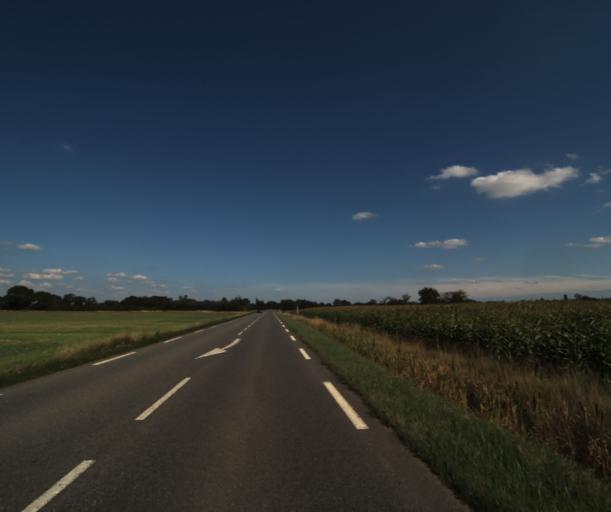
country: FR
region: Midi-Pyrenees
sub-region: Departement de la Haute-Garonne
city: Fonsorbes
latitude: 43.5096
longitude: 1.2293
